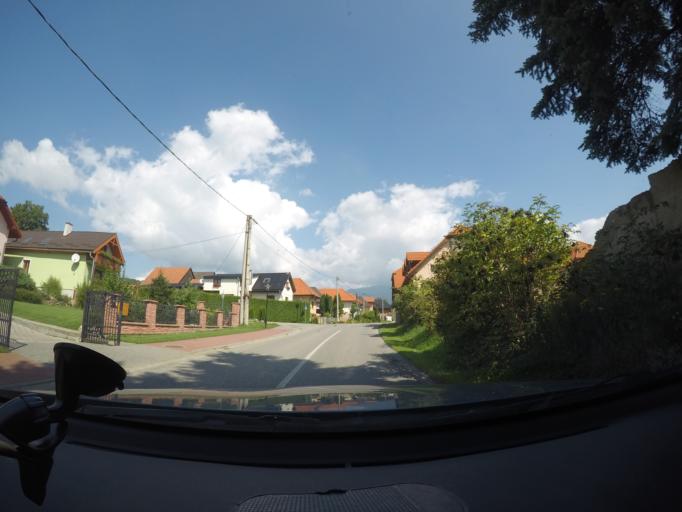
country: SK
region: Zilinsky
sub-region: Okres Liptovsky Mikulas
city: Liptovsky Mikulas
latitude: 49.1204
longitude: 19.6120
